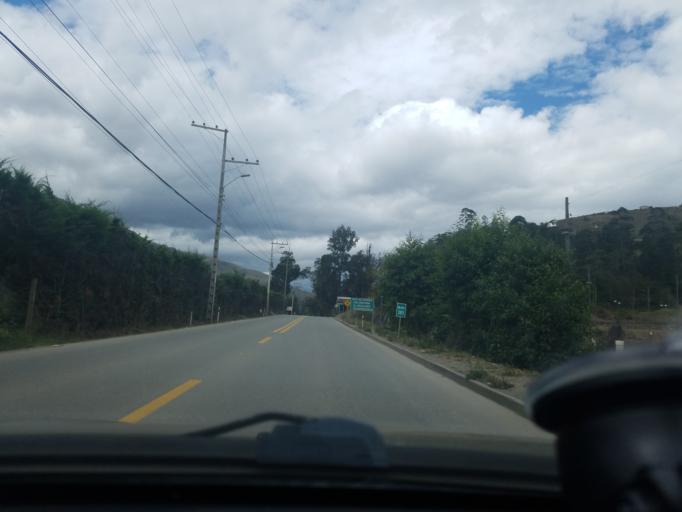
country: EC
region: Azuay
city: La Union
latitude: -2.8166
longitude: -78.7729
